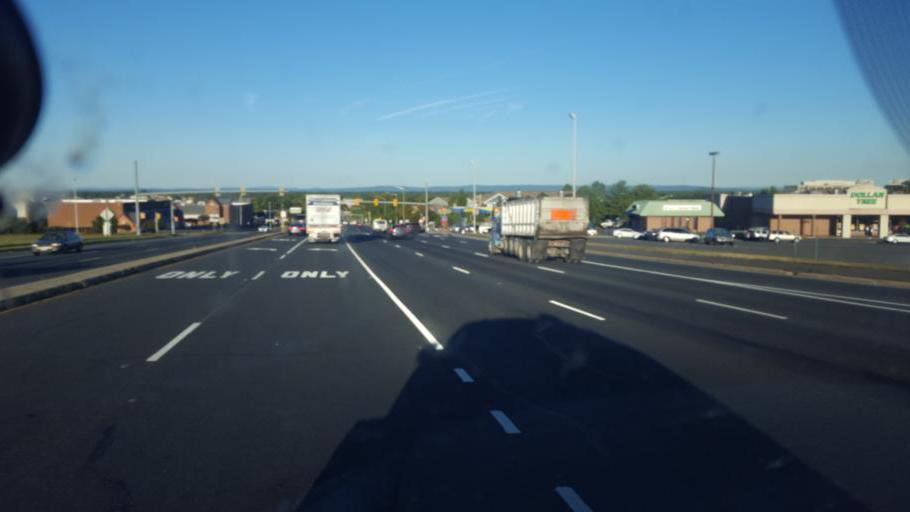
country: US
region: Virginia
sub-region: Fairfax County
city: Centreville
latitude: 38.8387
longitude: -77.4323
